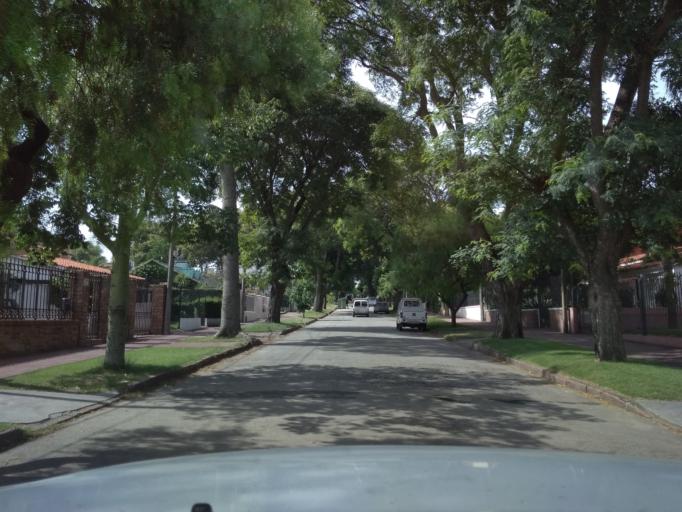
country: UY
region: Canelones
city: Paso de Carrasco
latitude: -34.8920
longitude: -56.0845
